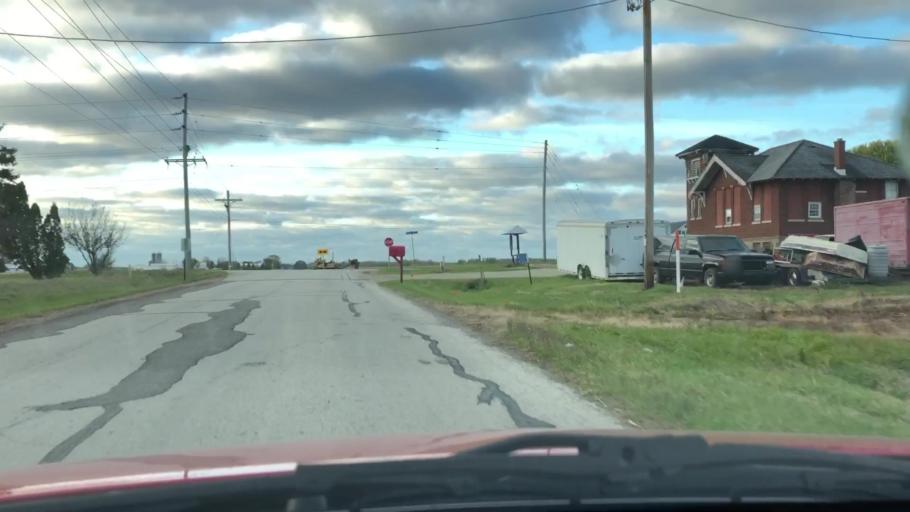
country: US
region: Wisconsin
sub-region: Outagamie County
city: Seymour
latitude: 44.5012
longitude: -88.3105
